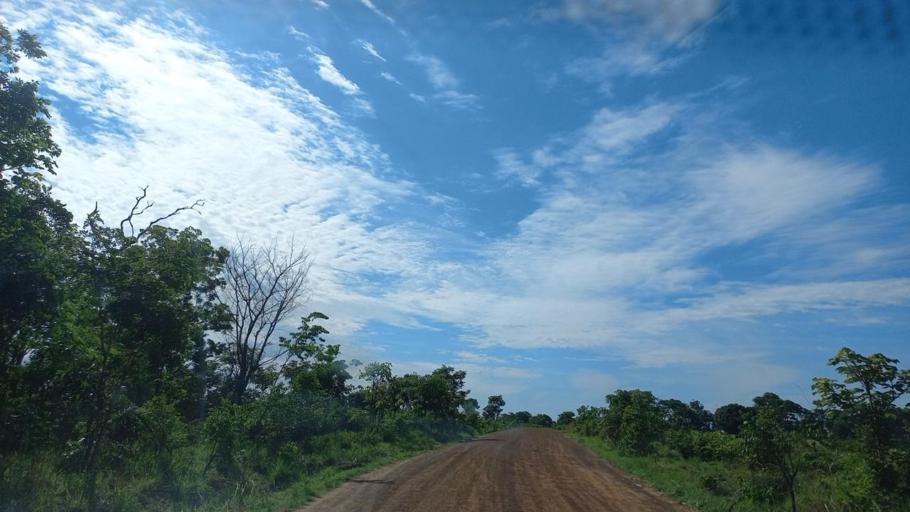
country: ZM
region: North-Western
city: Kabompo
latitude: -13.4313
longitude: 24.4182
